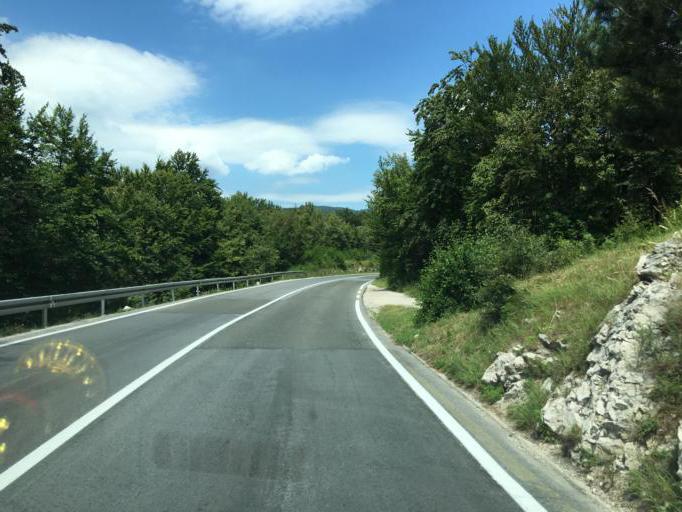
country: HR
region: Licko-Senjska
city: Jezerce
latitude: 44.9127
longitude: 15.6071
